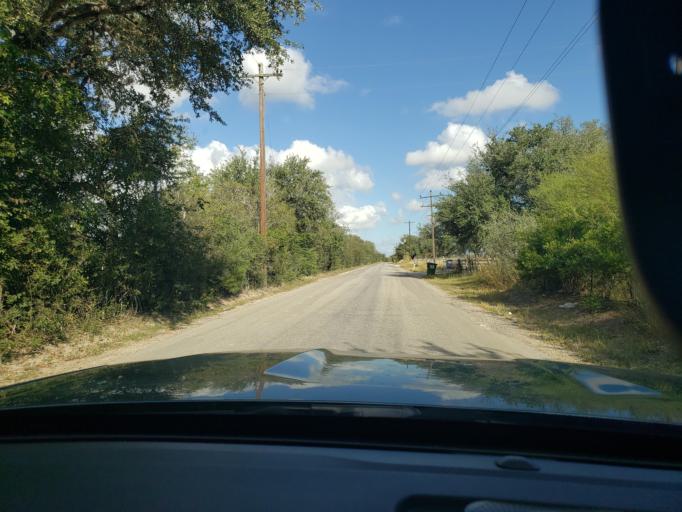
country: US
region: Texas
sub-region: Bee County
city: Beeville
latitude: 28.4442
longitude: -97.7150
